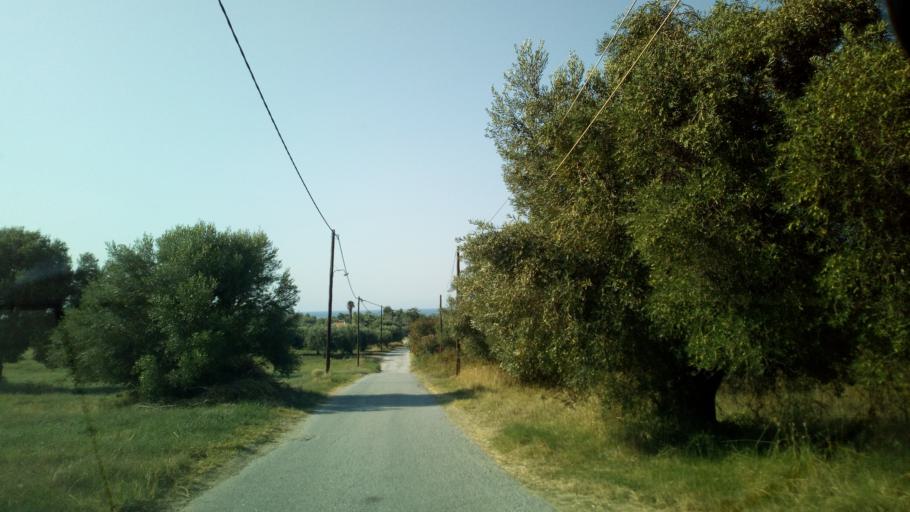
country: GR
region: Central Macedonia
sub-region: Nomos Chalkidikis
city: Pefkochori
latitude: 39.9743
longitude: 23.6527
